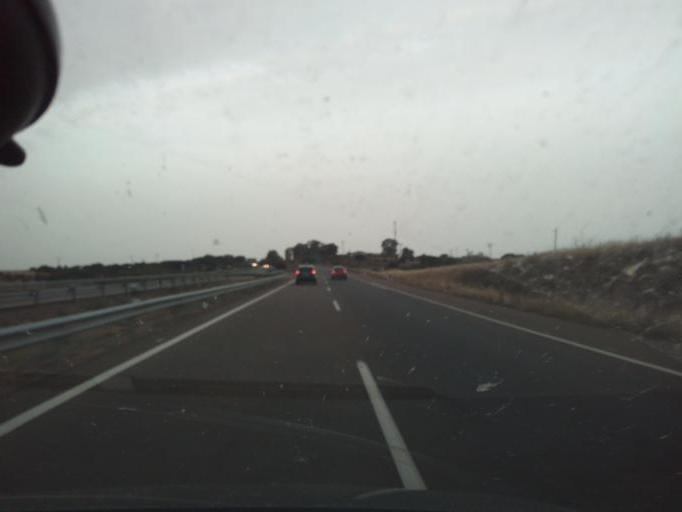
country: ES
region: Extremadura
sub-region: Provincia de Badajoz
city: San Pedro de Merida
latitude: 38.9488
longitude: -6.1954
